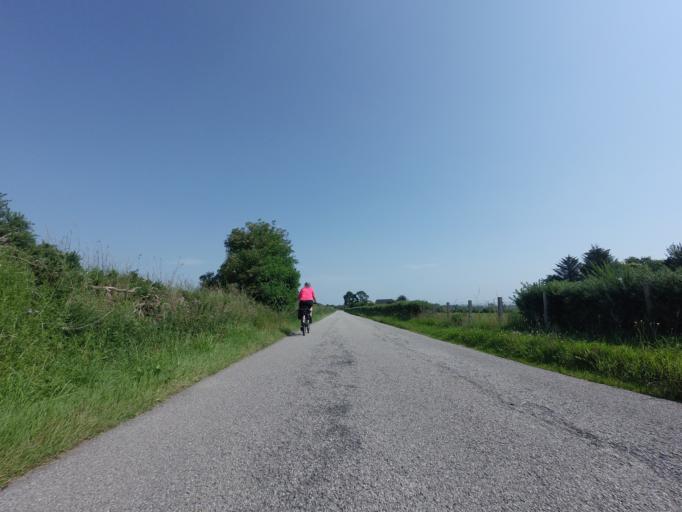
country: GB
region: Scotland
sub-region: Highland
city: Tain
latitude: 57.7975
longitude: -4.0713
